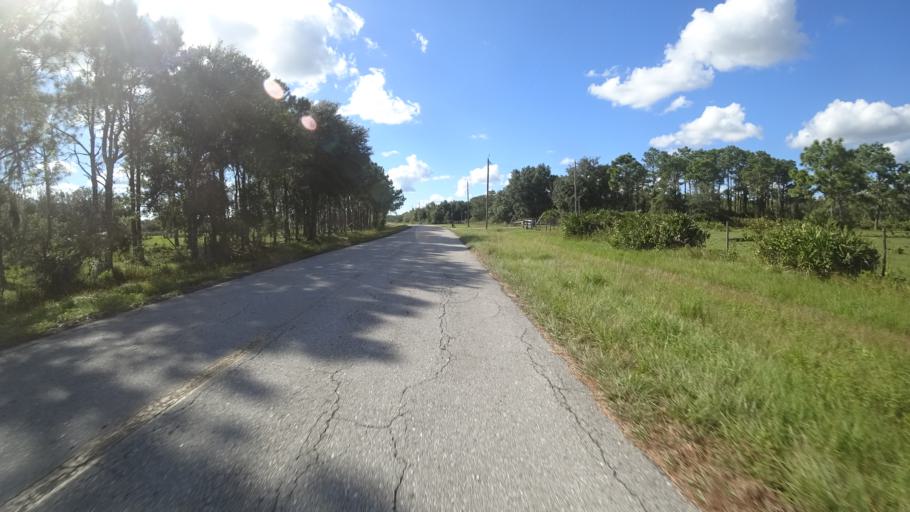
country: US
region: Florida
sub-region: Sarasota County
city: Warm Mineral Springs
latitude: 27.2741
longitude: -82.1183
